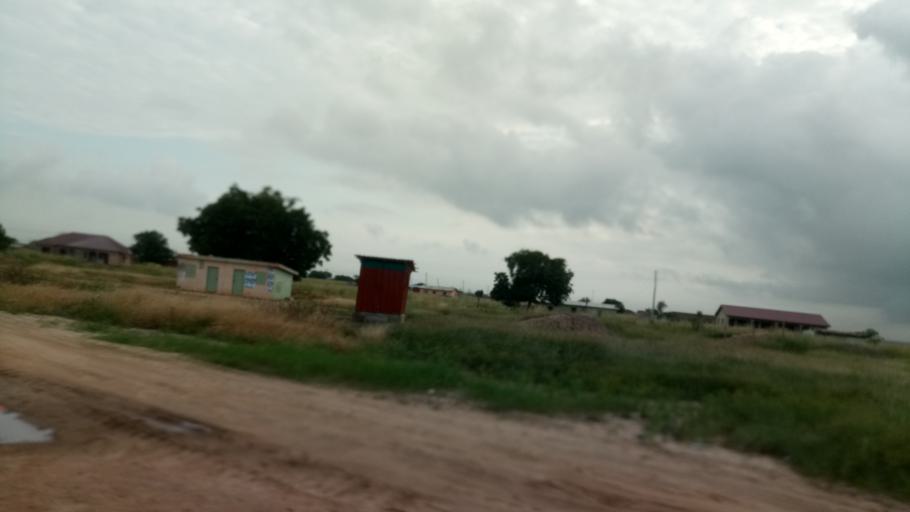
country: GH
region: Greater Accra
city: Tema
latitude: 5.8724
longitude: 0.3409
